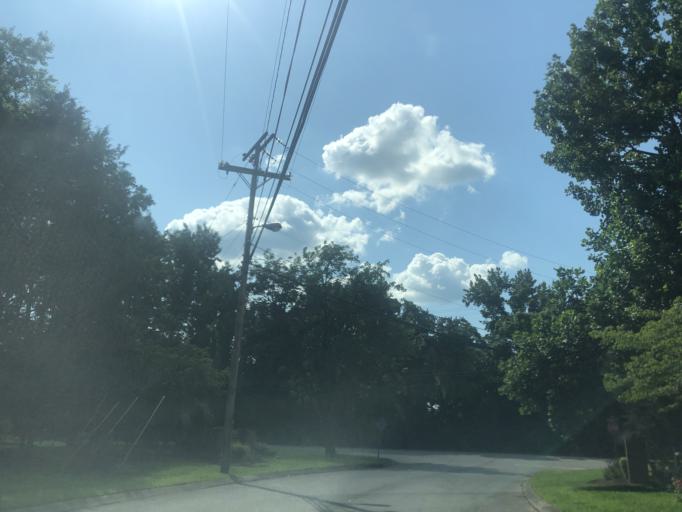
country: US
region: Tennessee
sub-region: Wilson County
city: Green Hill
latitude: 36.1932
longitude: -86.6004
